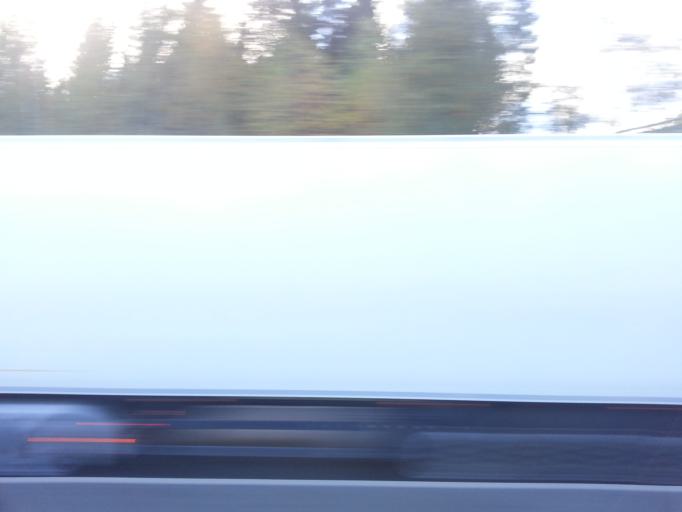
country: NO
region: Sor-Trondelag
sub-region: Malvik
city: Hommelvik
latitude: 63.4134
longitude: 10.7694
